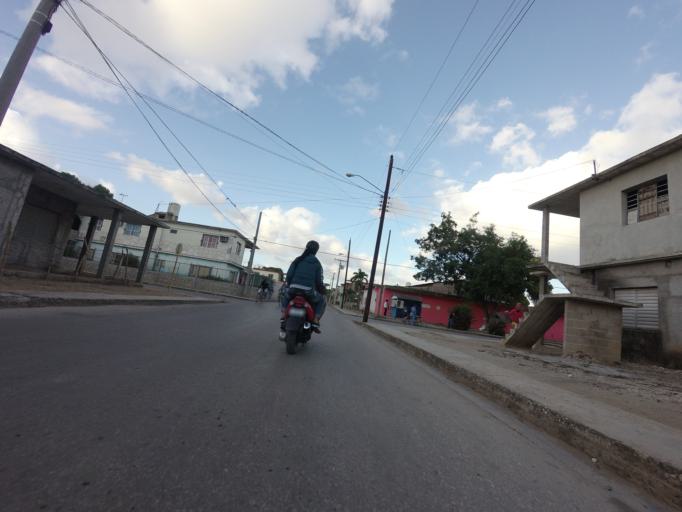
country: CU
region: Ciego de Avila
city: Ciego de Avila
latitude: 21.8360
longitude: -78.7562
